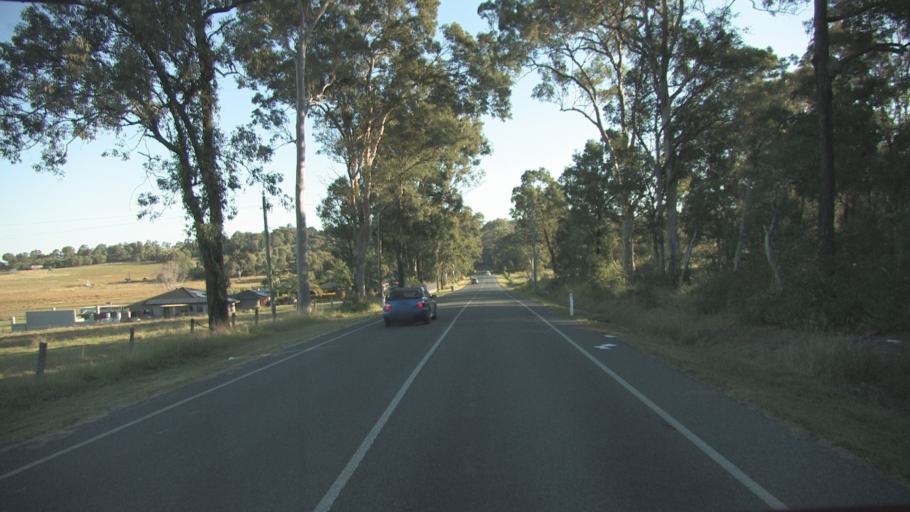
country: AU
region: Queensland
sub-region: Logan
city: Logan Reserve
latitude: -27.7200
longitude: 153.1110
